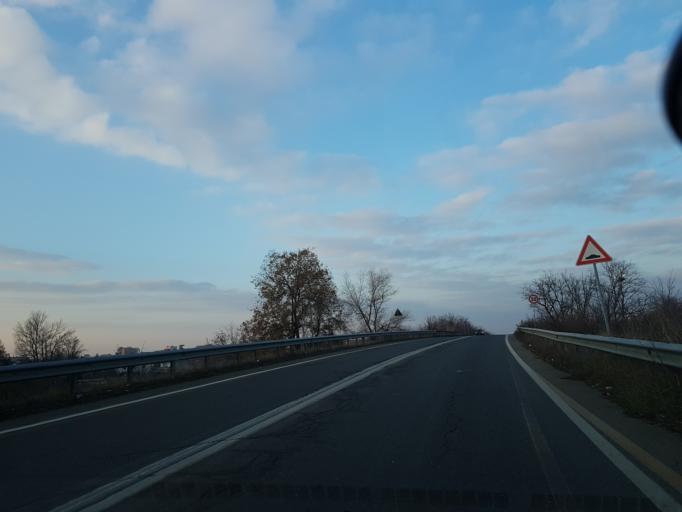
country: IT
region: Piedmont
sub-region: Provincia di Alessandria
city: Novi Ligure
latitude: 44.7513
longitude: 8.8081
